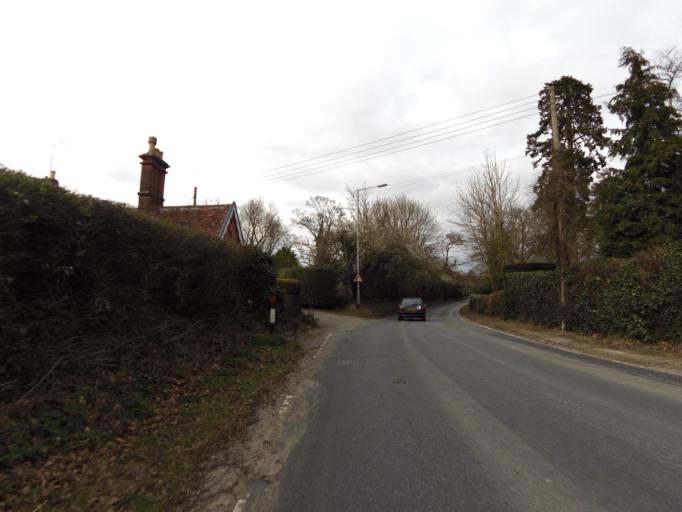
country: GB
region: England
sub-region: Suffolk
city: Ipswich
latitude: 52.0860
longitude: 1.1495
